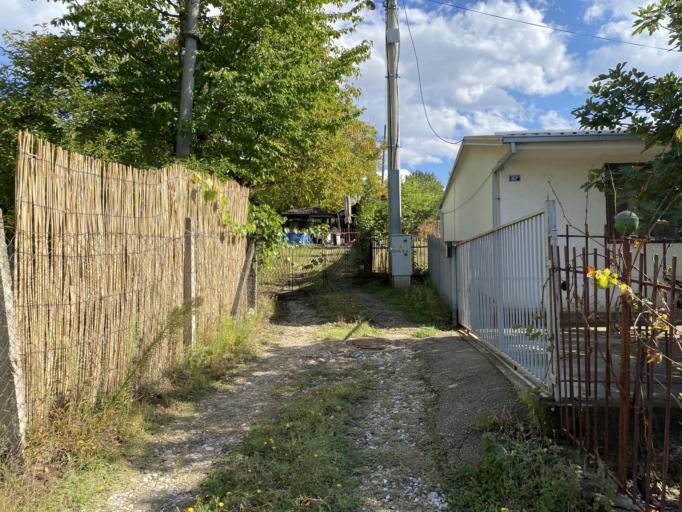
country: MK
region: Suto Orizari
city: Suto Orizare
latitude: 42.0337
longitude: 21.4101
